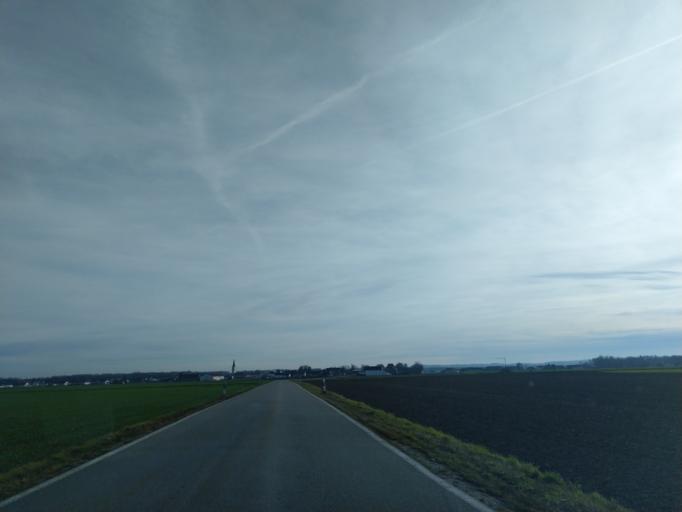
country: DE
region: Bavaria
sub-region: Lower Bavaria
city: Otzing
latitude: 48.7499
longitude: 12.8166
